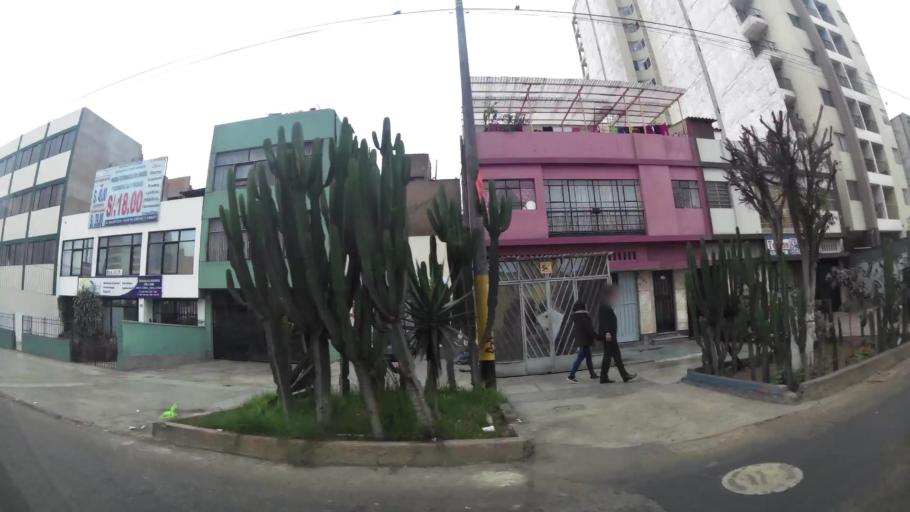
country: PE
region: Lima
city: Lima
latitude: -12.0696
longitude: -77.0494
